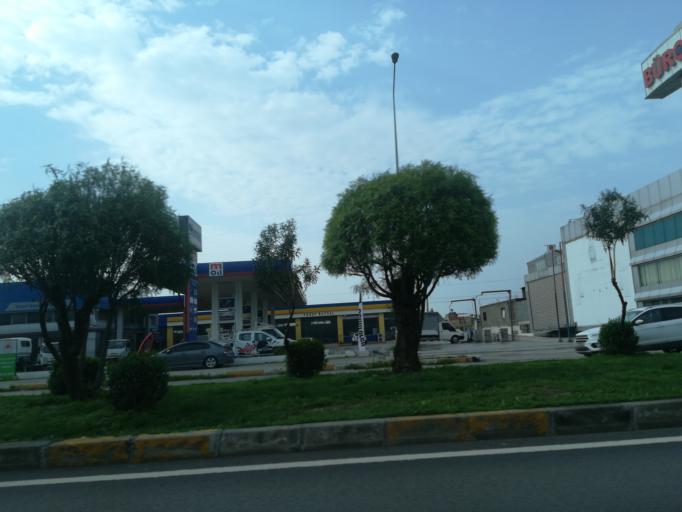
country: TR
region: Adana
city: Yuregir
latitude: 36.9856
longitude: 35.3650
